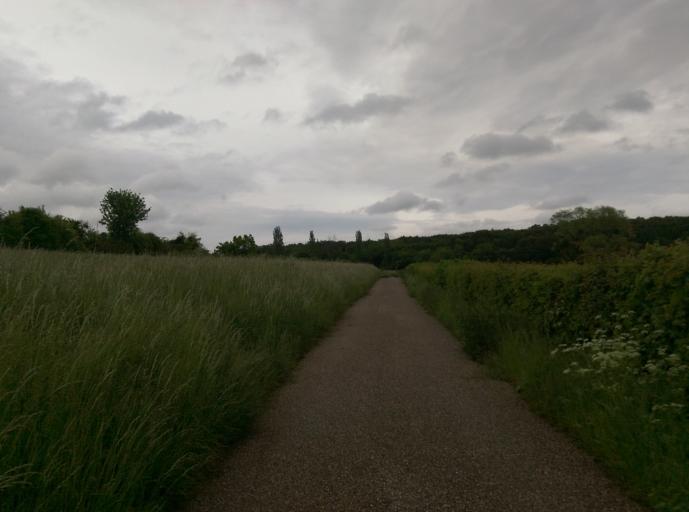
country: LU
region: Luxembourg
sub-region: Canton de Luxembourg
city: Niederanven
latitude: 49.6619
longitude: 6.2550
